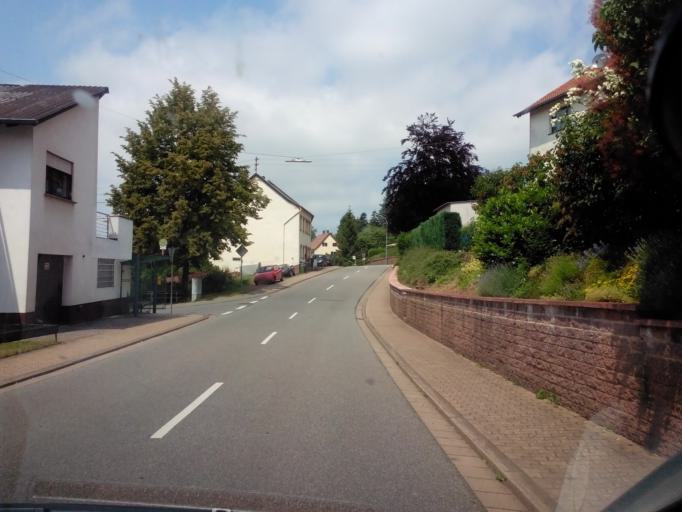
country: DE
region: Saarland
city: Eppelborn
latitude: 49.3957
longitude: 6.9917
